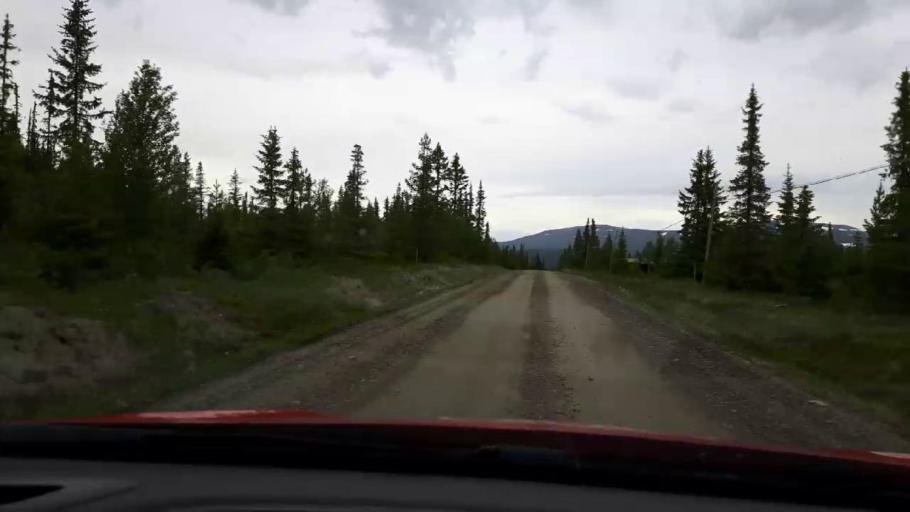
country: SE
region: Jaemtland
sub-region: Are Kommun
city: Are
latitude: 62.8353
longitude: 12.8051
